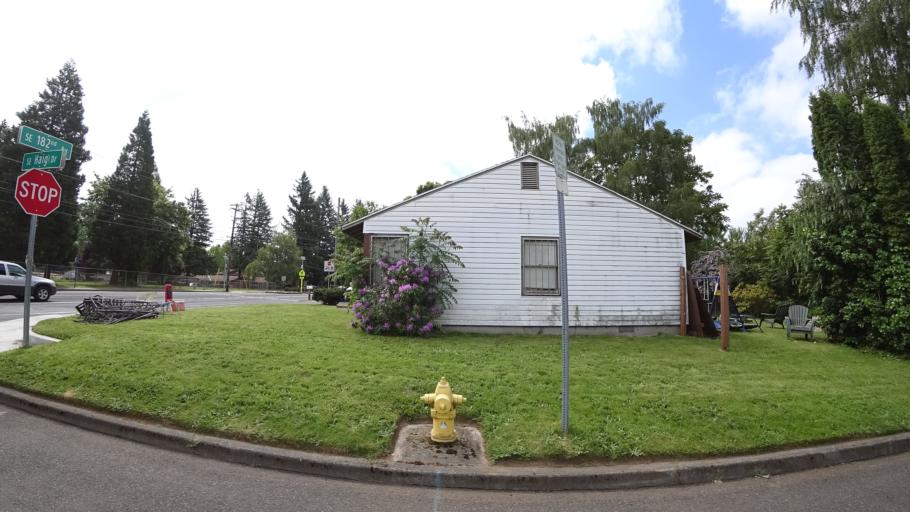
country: US
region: Oregon
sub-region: Multnomah County
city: Gresham
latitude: 45.4976
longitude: -122.4759
